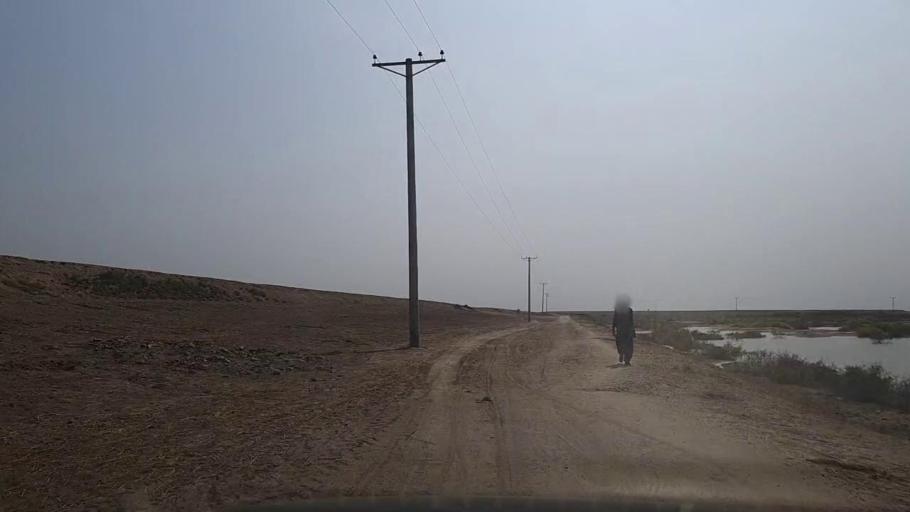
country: PK
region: Sindh
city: Thatta
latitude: 24.5771
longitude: 67.9157
